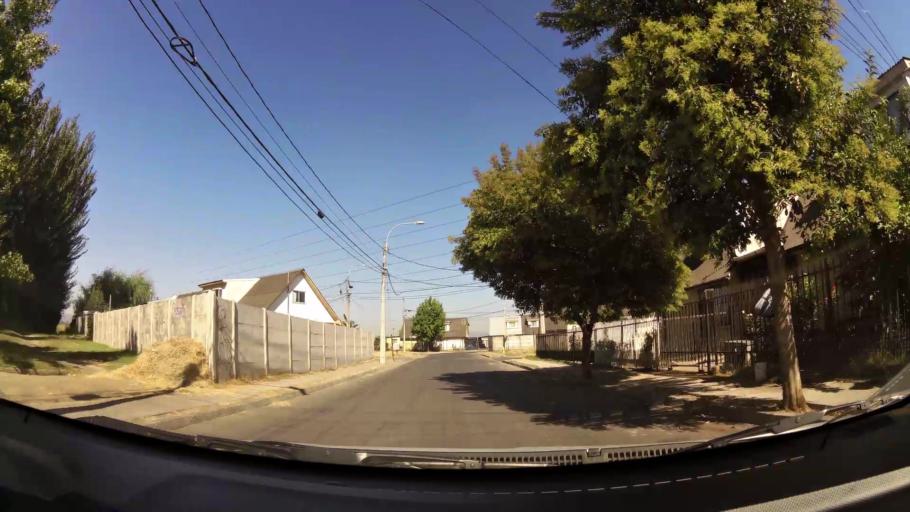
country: CL
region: Maule
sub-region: Provincia de Curico
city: Curico
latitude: -34.9800
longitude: -71.2666
